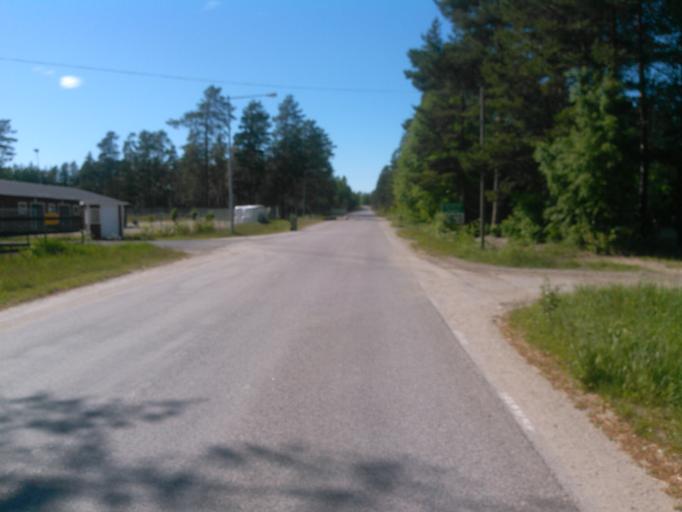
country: SE
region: Vaesterbotten
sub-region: Umea Kommun
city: Roback
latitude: 63.8240
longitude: 20.1793
